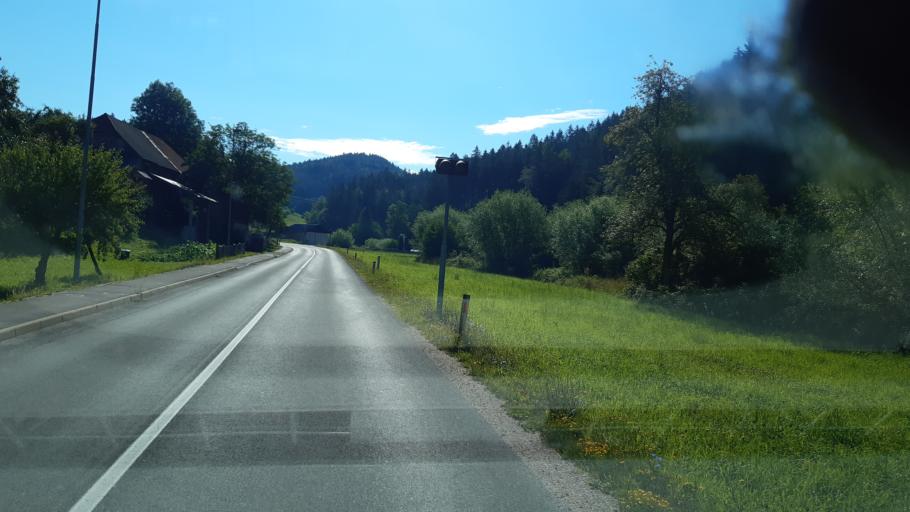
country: SI
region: Lukovica
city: Lukovica pri Domzalah
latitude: 46.2144
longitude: 14.7318
